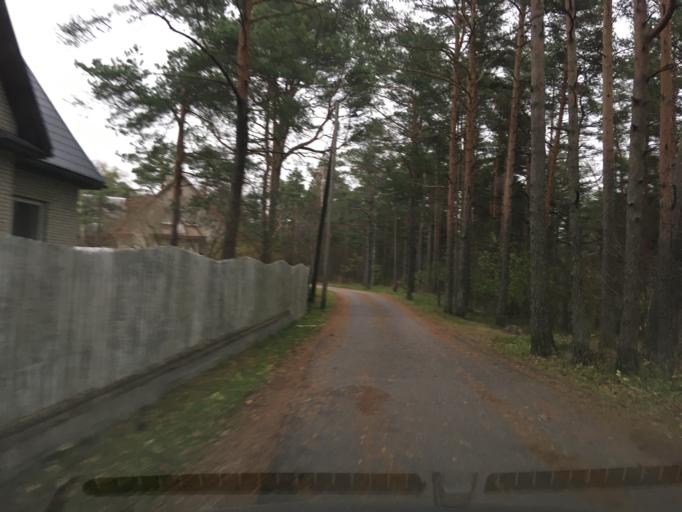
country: EE
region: Harju
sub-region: Tallinna linn
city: Tallinn
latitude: 59.3748
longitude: 24.6985
